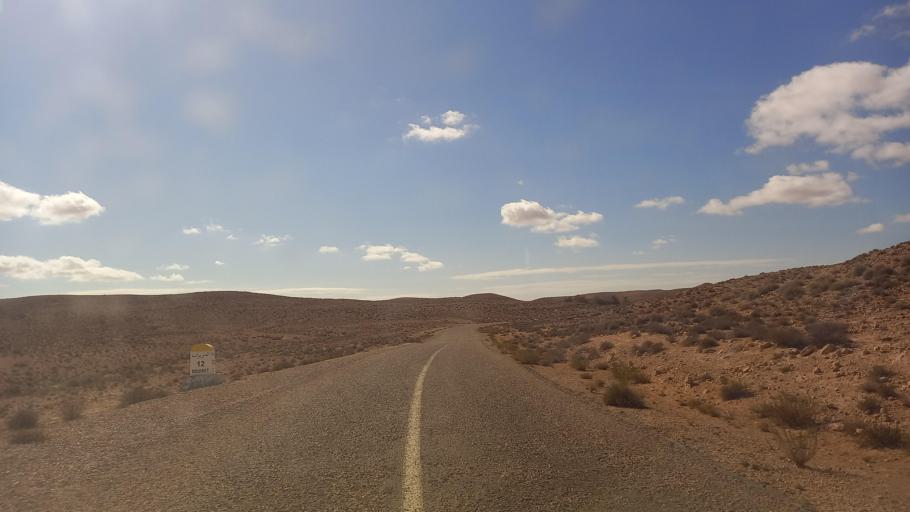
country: TN
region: Tataouine
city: Tataouine
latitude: 32.8788
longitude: 10.2400
